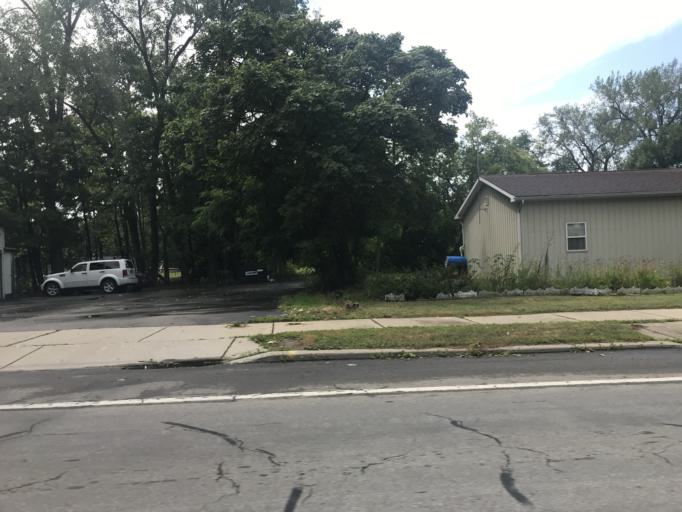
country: US
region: New York
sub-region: Chautauqua County
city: Silver Creek
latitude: 42.5447
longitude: -79.1688
